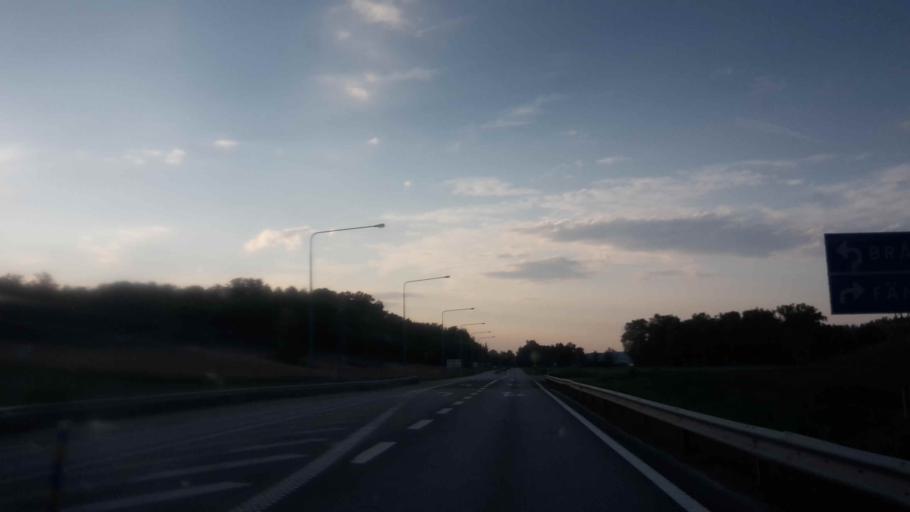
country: SE
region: OEstergoetland
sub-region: Valdemarsviks Kommun
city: Gusum
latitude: 58.3166
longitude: 16.4797
